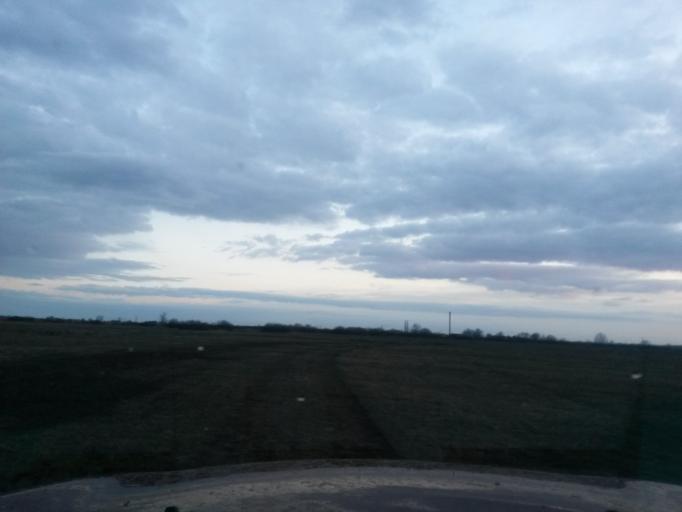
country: SK
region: Kosicky
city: Sobrance
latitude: 48.6958
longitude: 22.0551
